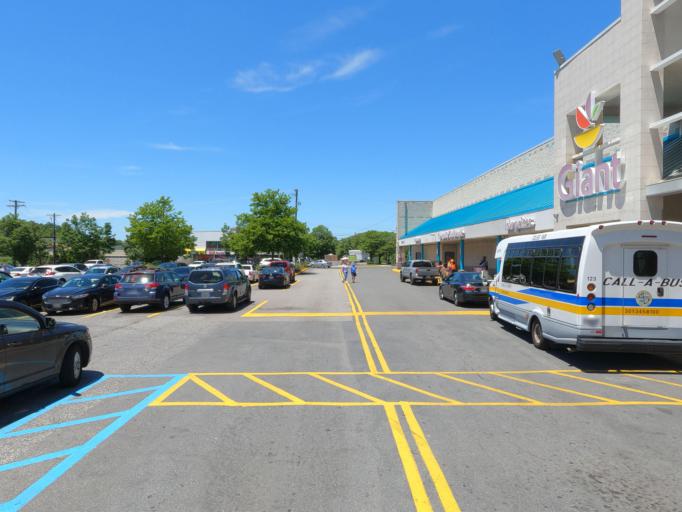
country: US
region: Maryland
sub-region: Prince George's County
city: Berwyn Heights
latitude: 38.9989
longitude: -76.9108
